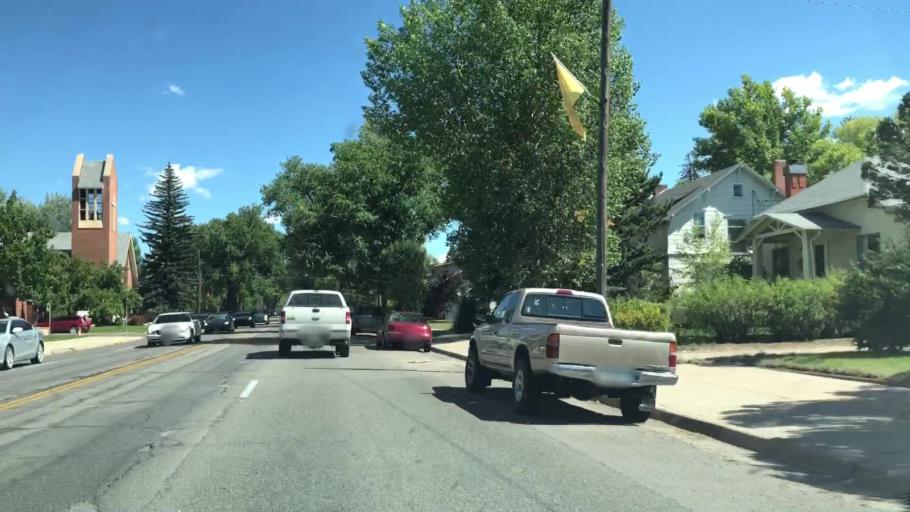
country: US
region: Wyoming
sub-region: Albany County
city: Laramie
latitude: 41.3104
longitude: -105.5840
